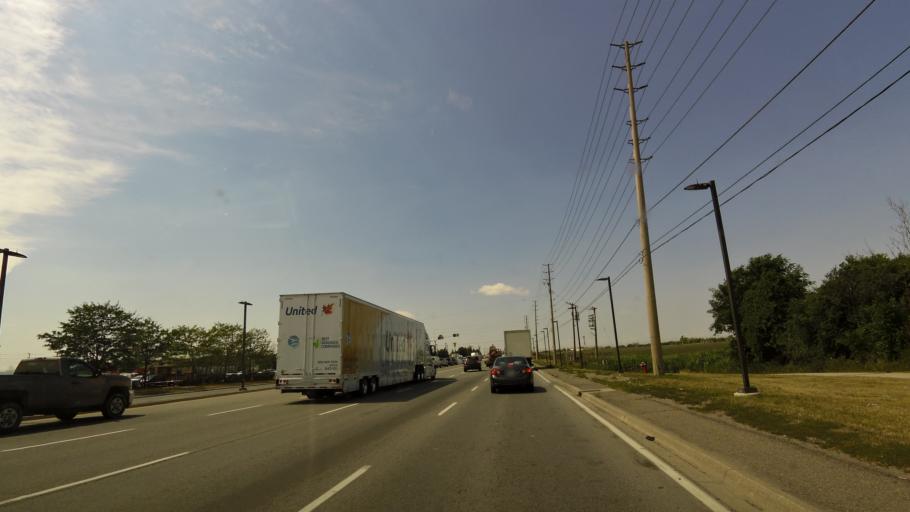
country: CA
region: Ontario
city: Mississauga
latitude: 43.6671
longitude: -79.6633
